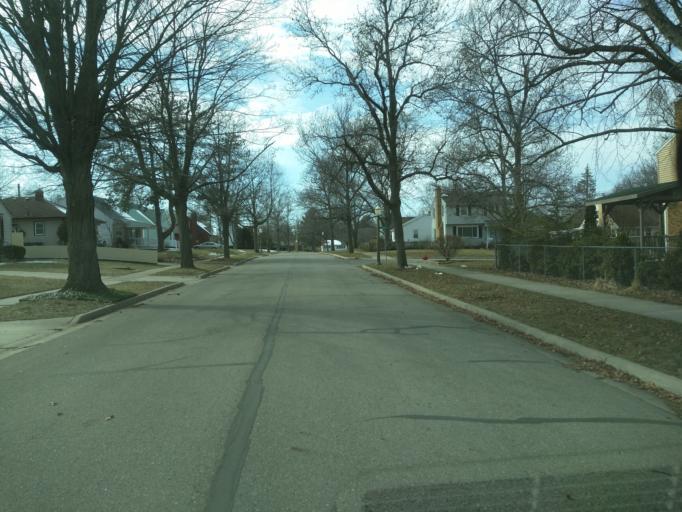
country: US
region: Michigan
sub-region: Ingham County
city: Lansing
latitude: 42.7066
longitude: -84.5784
